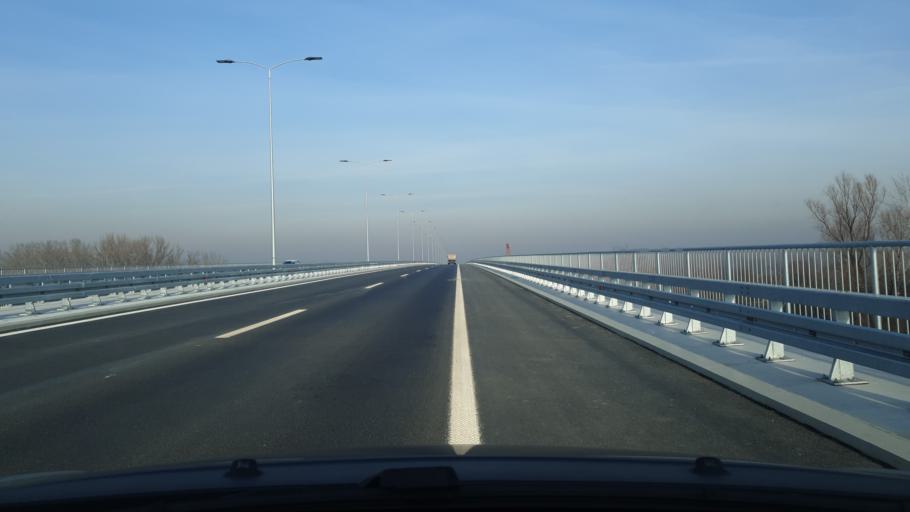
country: RS
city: Baric
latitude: 44.6622
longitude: 20.2422
